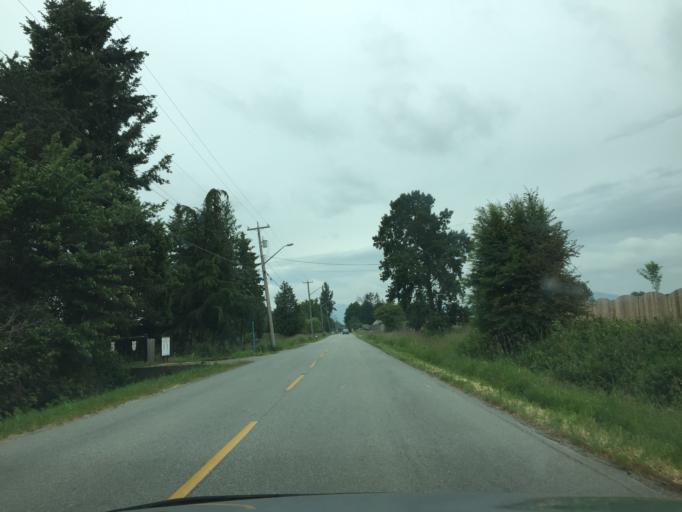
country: CA
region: British Columbia
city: Richmond
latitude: 49.1513
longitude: -123.0806
